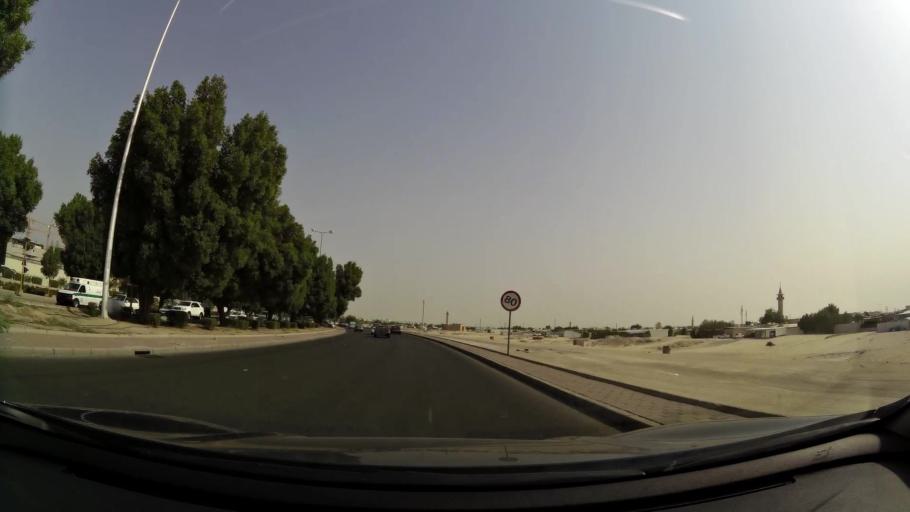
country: KW
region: Muhafazat al Jahra'
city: Al Jahra'
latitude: 29.3355
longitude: 47.6771
